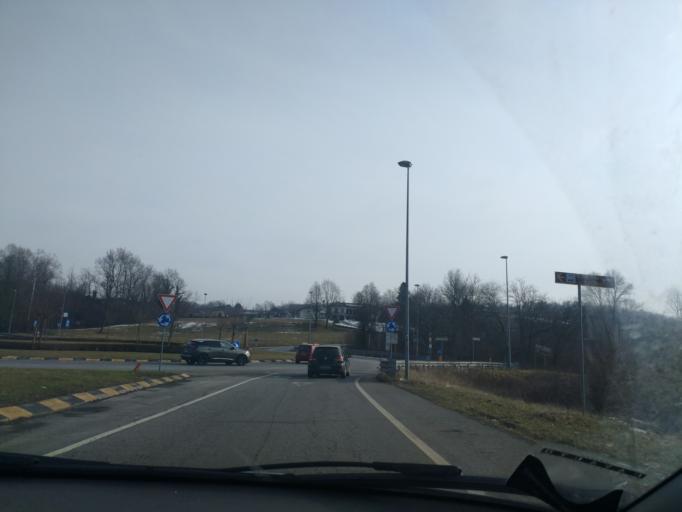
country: IT
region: Lombardy
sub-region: Provincia di Como
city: Lurago d'Erba
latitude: 45.7589
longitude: 9.2096
